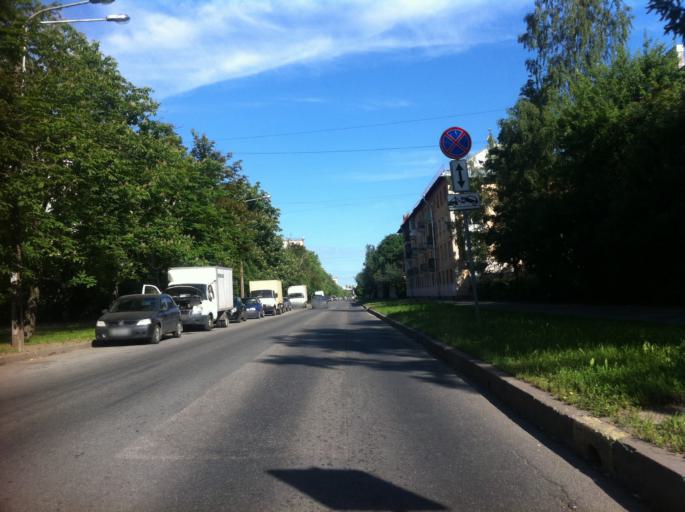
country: RU
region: St.-Petersburg
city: Dachnoye
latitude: 59.8353
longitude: 30.2558
